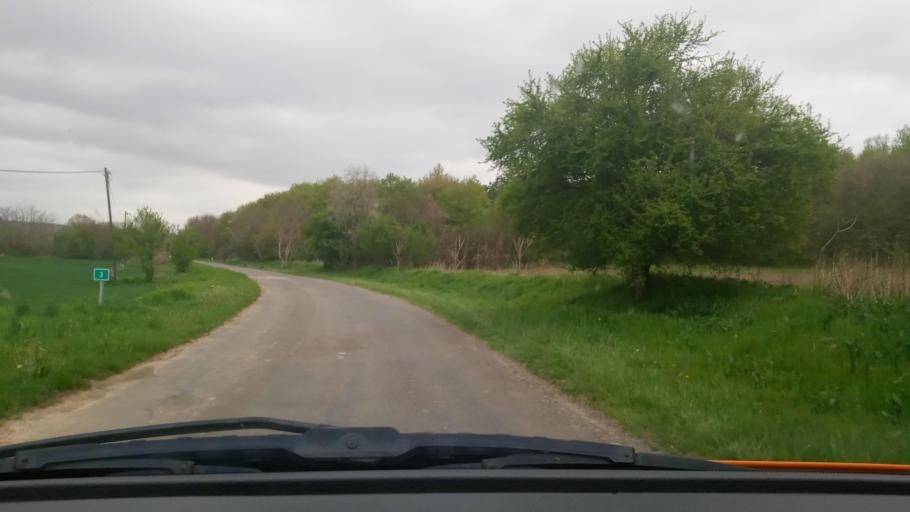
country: HU
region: Baranya
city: Boly
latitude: 46.0123
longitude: 18.5456
